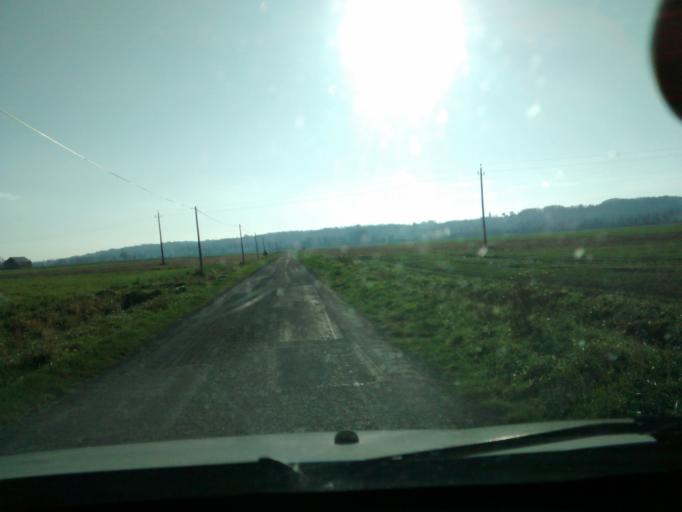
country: FR
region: Brittany
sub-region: Departement d'Ille-et-Vilaine
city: Roz-sur-Couesnon
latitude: 48.6080
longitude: -1.5820
